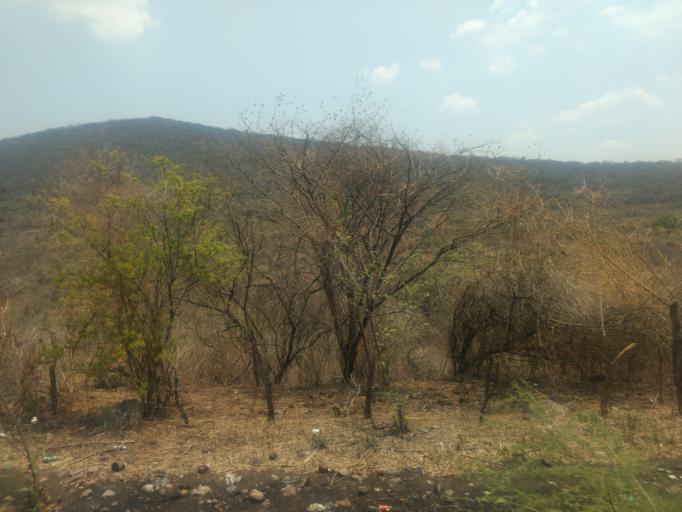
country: MX
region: Morelos
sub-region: Mazatepec
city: Cuauchichinola
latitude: 18.6513
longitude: -99.4008
